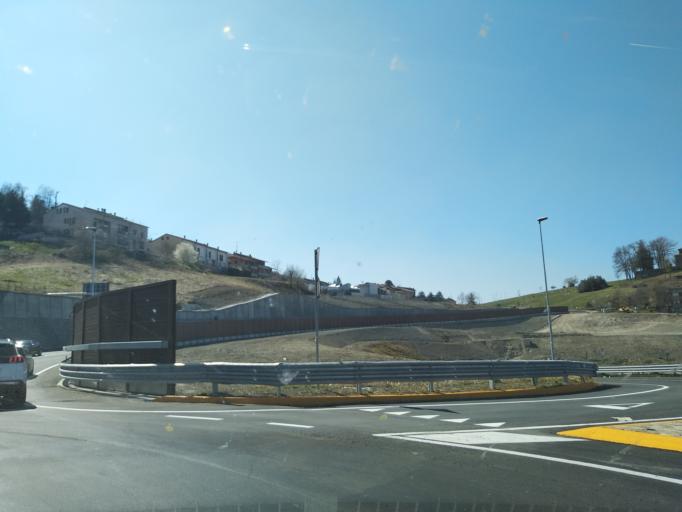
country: IT
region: Emilia-Romagna
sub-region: Provincia di Reggio Emilia
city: Castelnovo ne'Monti
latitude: 44.4335
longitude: 10.4162
